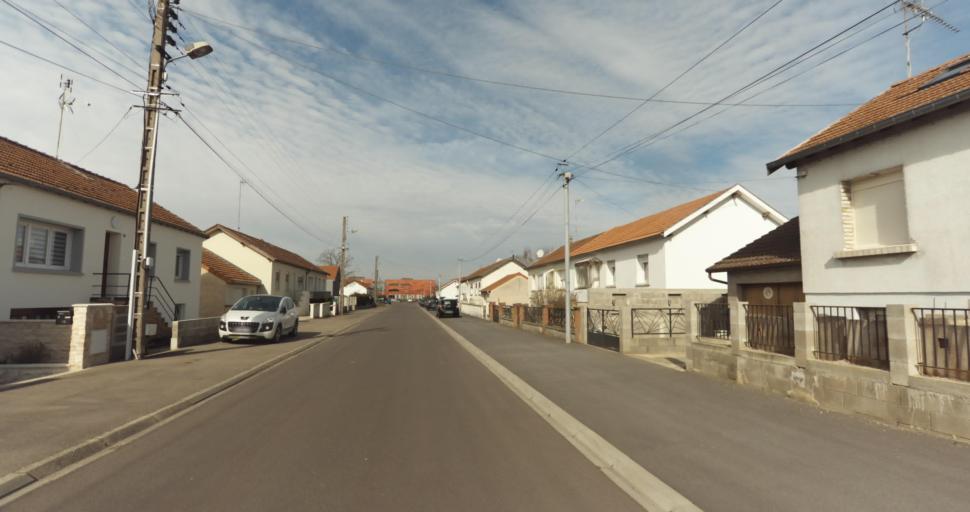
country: FR
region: Lorraine
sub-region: Departement de Meurthe-et-Moselle
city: Jarny
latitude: 49.1549
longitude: 5.8790
